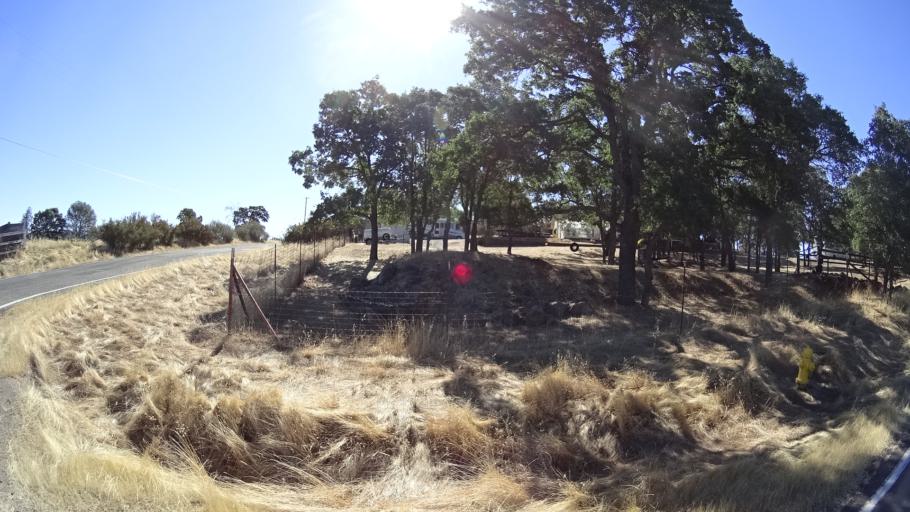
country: US
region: California
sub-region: Calaveras County
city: Rancho Calaveras
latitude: 38.1136
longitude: -120.8596
